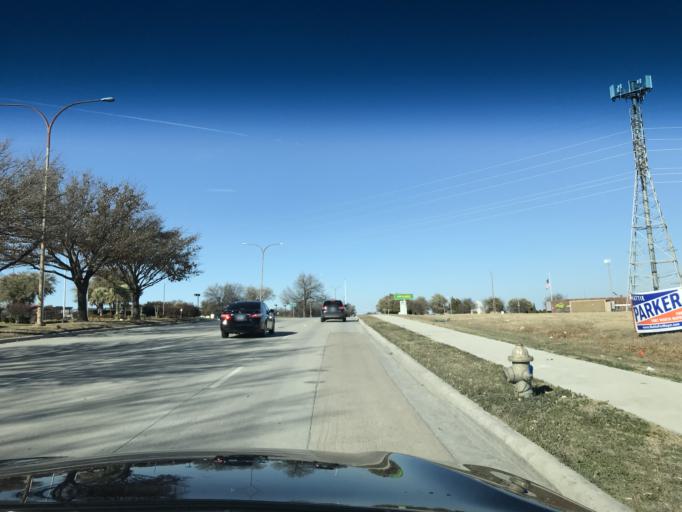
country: US
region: Texas
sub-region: Tarrant County
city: Benbrook
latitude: 32.6735
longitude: -97.4185
